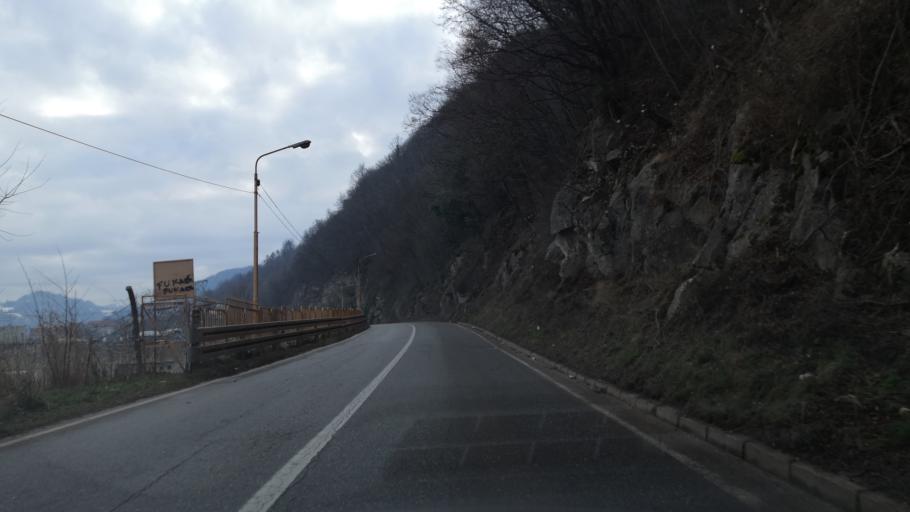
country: RS
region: Central Serbia
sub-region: Macvanski Okrug
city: Mali Zvornik
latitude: 44.3675
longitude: 19.1036
